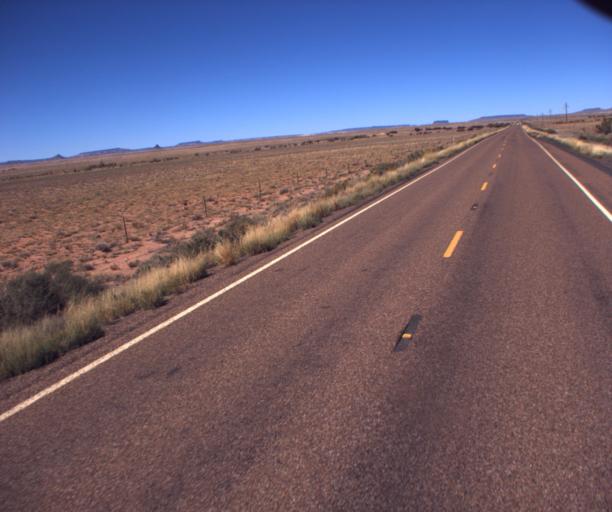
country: US
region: Arizona
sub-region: Navajo County
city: Holbrook
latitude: 35.0731
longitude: -110.0999
